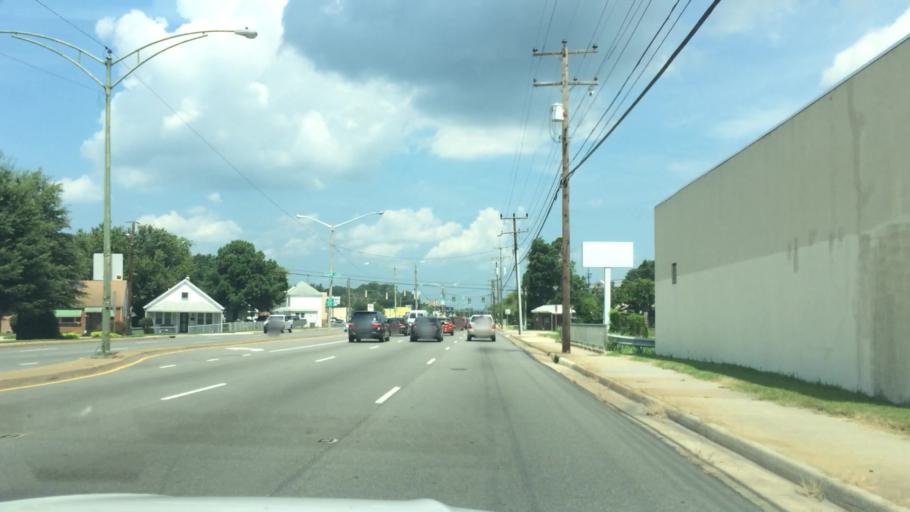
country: US
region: Virginia
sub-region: City of Newport News
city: Newport News
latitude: 37.0261
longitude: -76.4486
